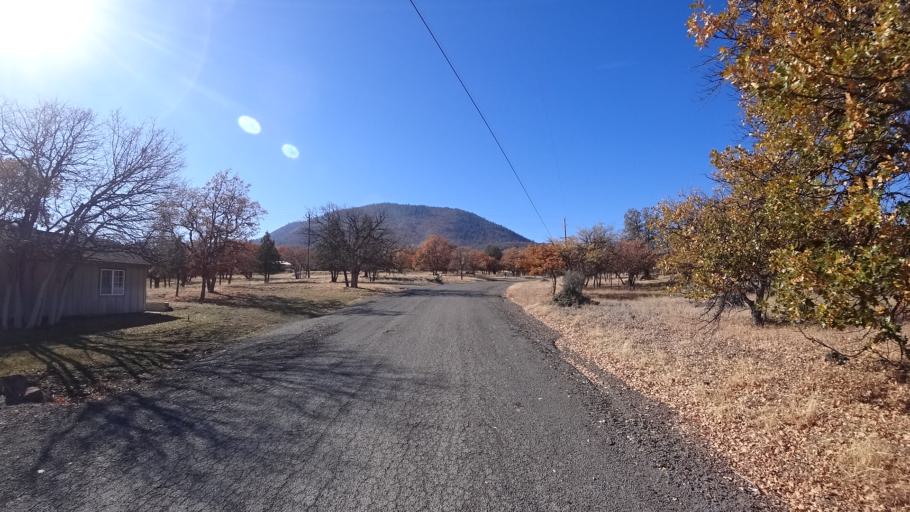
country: US
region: California
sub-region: Siskiyou County
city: Montague
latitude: 41.8793
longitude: -122.4829
